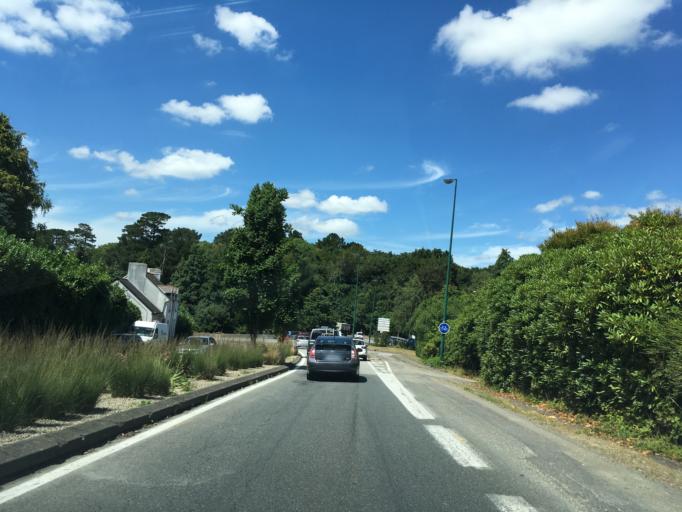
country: FR
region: Brittany
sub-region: Departement du Finistere
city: Quimper
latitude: 47.9720
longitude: -4.0869
